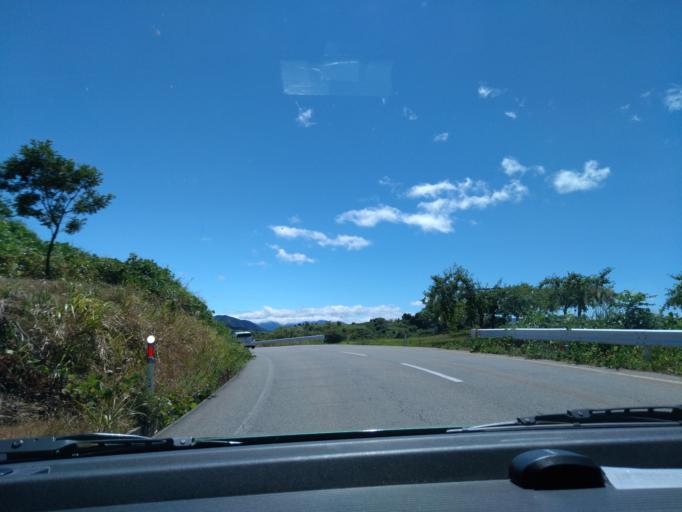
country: JP
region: Akita
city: Yuzawa
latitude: 39.2267
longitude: 140.5642
